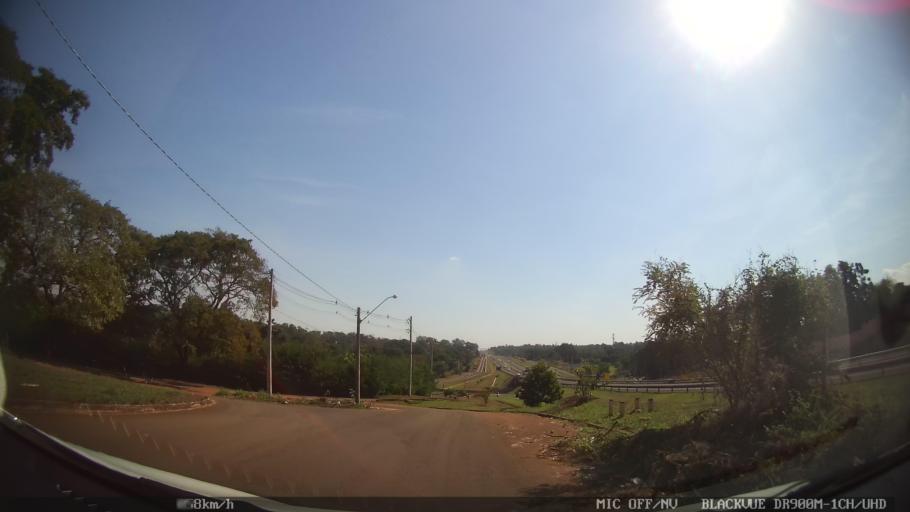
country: BR
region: Sao Paulo
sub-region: Ribeirao Preto
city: Ribeirao Preto
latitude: -21.2175
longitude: -47.8337
